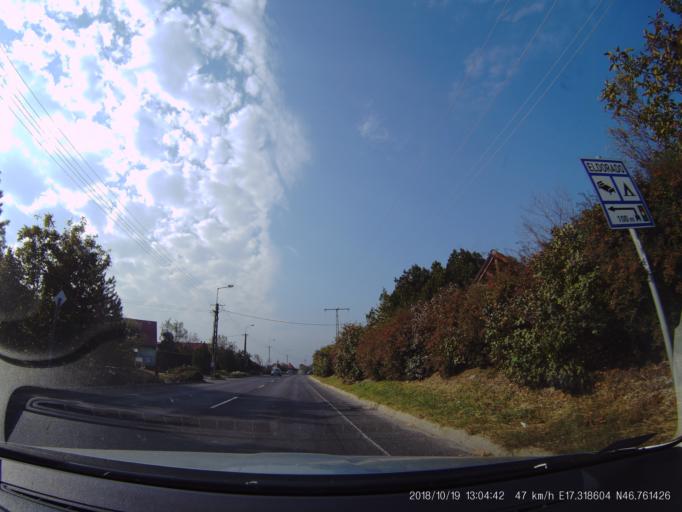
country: HU
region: Zala
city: Vonyarcvashegy
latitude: 46.7614
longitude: 17.3186
